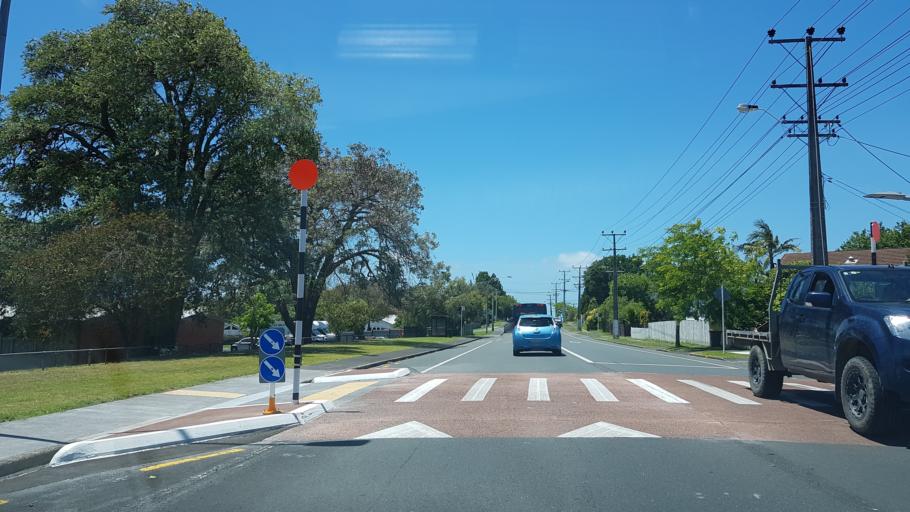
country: NZ
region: Auckland
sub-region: Auckland
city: North Shore
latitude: -36.7802
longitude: 174.7326
